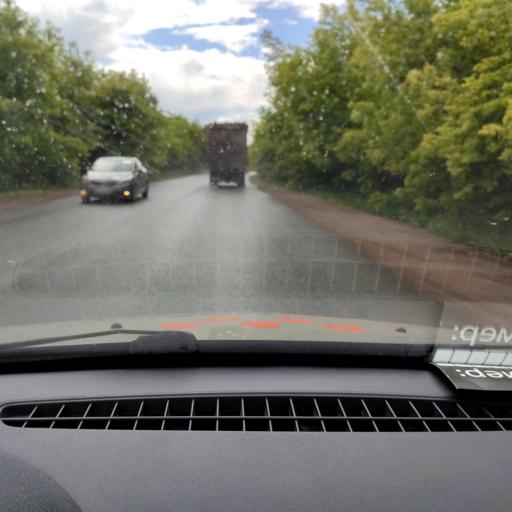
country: RU
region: Bashkortostan
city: Iglino
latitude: 54.7763
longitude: 56.2506
